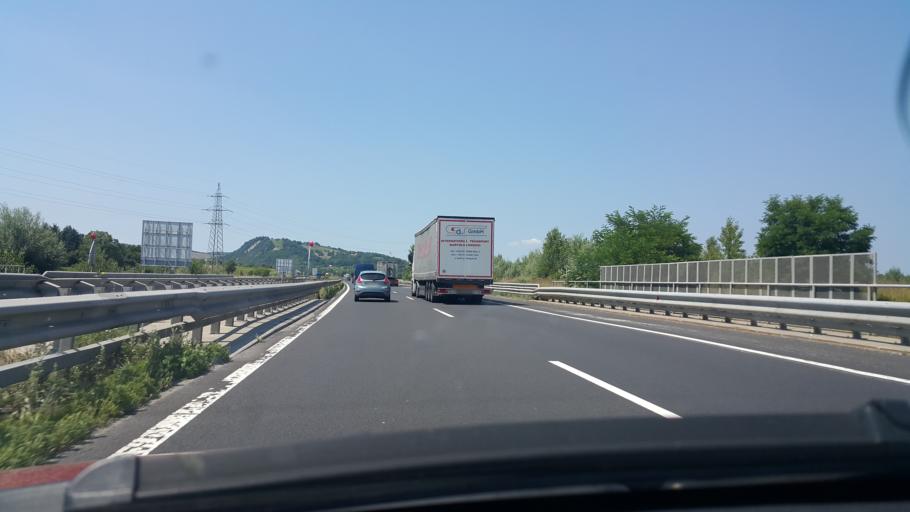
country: SI
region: Miklavz na Dravskem Polju
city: Miklavz na Dravskem Polju
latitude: 46.5409
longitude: 15.6983
